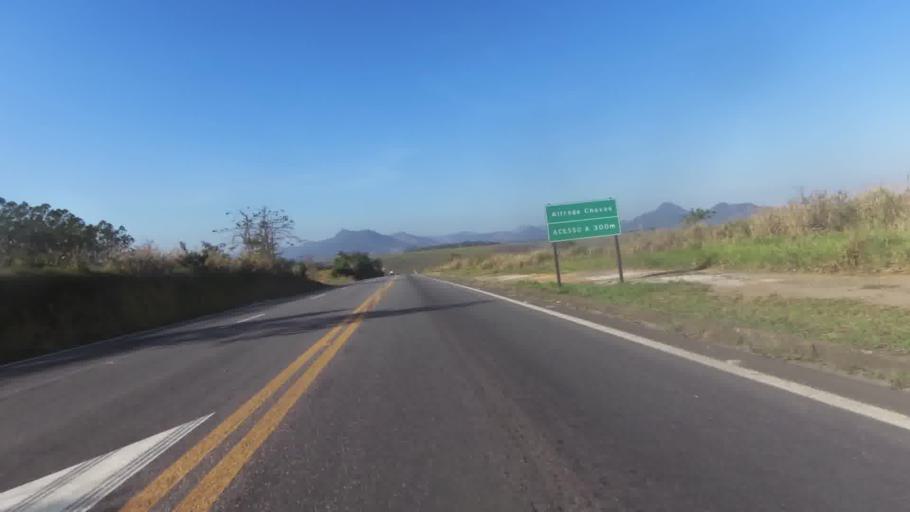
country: BR
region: Espirito Santo
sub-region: Alfredo Chaves
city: Alfredo Chaves
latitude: -20.6945
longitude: -40.7072
